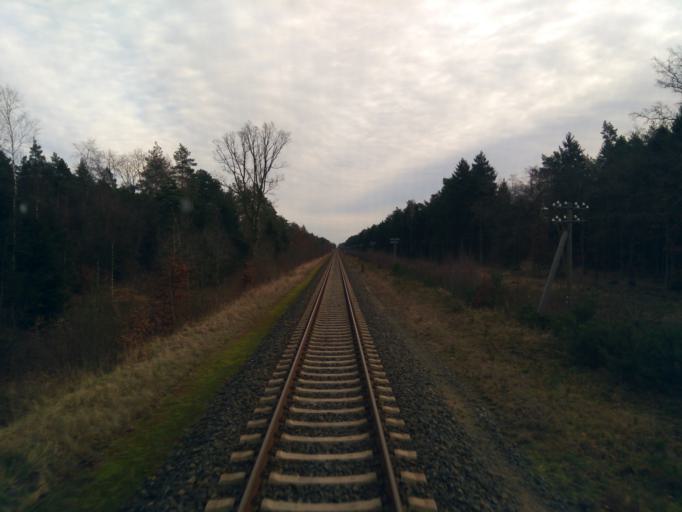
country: DE
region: Lower Saxony
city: Fassberg
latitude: 52.9957
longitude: 10.1882
